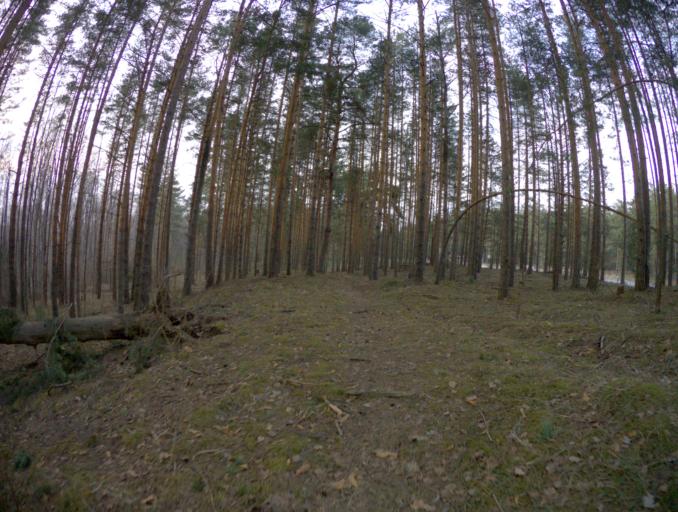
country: RU
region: Vladimir
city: Kommunar
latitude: 56.0713
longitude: 40.4319
